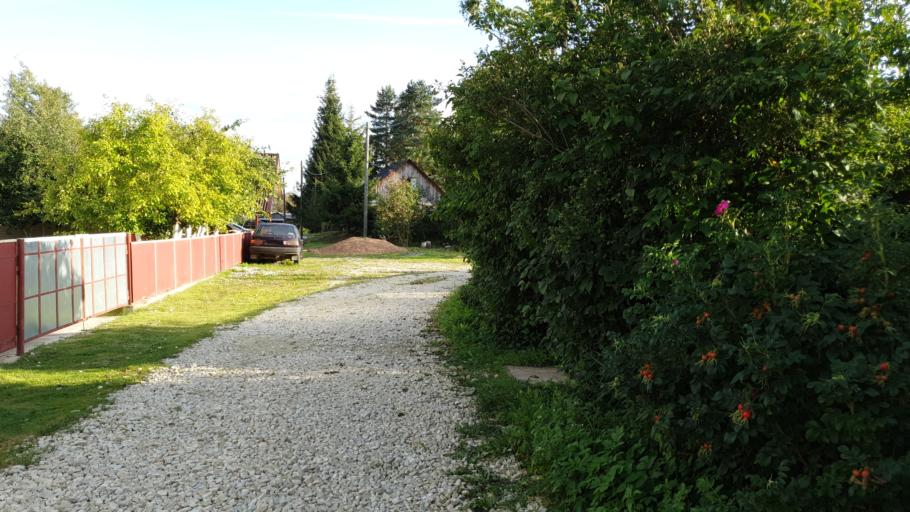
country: RU
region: Leningrad
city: Ivangorod
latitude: 59.4298
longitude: 28.3214
